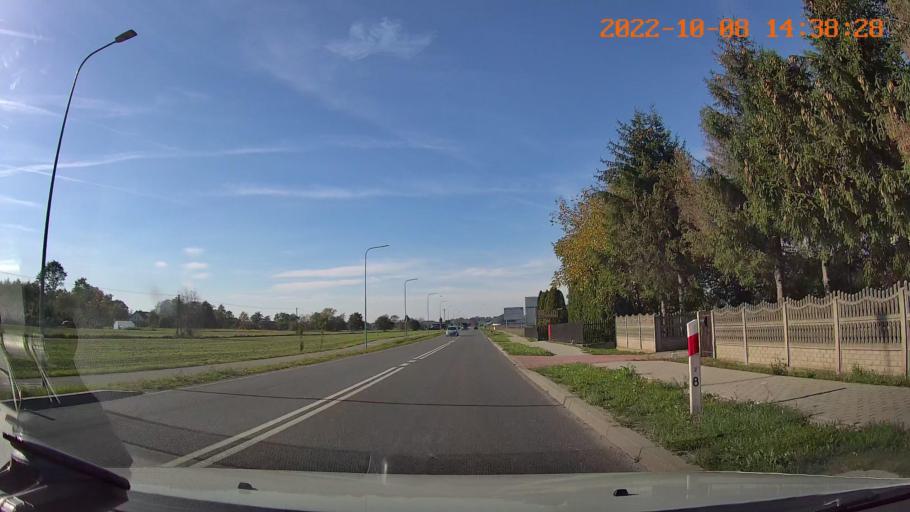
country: PL
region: Subcarpathian Voivodeship
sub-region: Powiat debicki
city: Zyrakow
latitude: 50.0724
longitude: 21.3928
